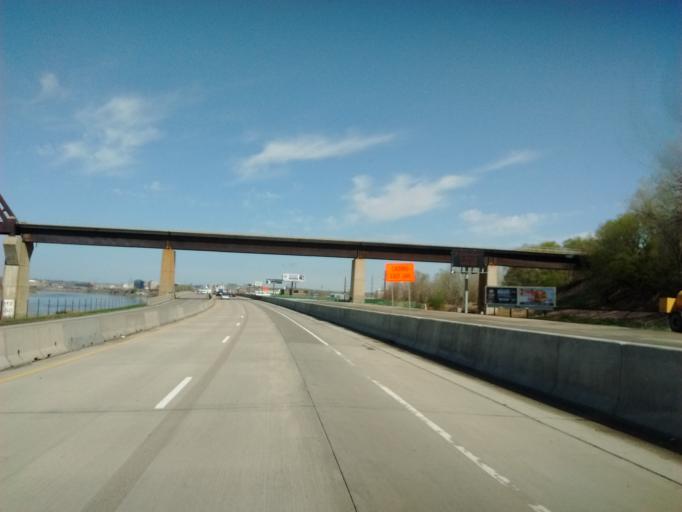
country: US
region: Nebraska
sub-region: Dakota County
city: South Sioux City
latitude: 42.4740
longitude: -96.3831
